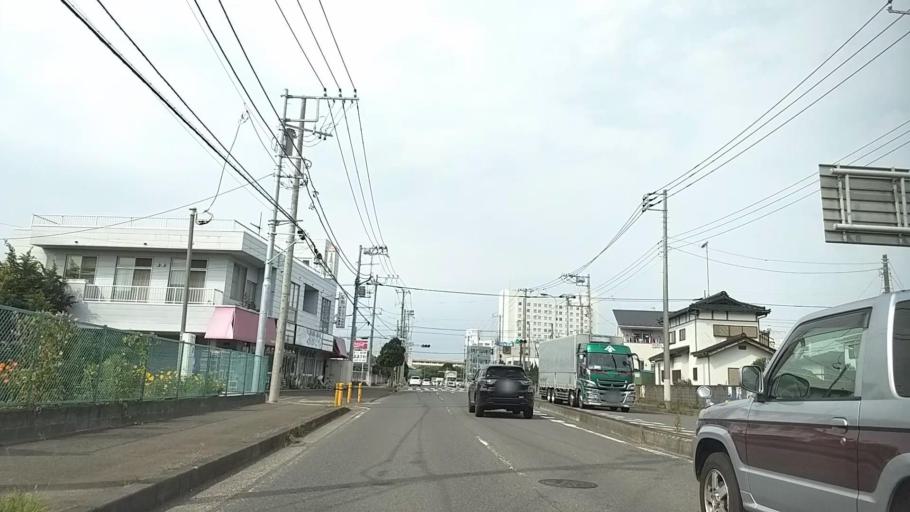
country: JP
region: Kanagawa
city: Atsugi
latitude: 35.4277
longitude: 139.3822
